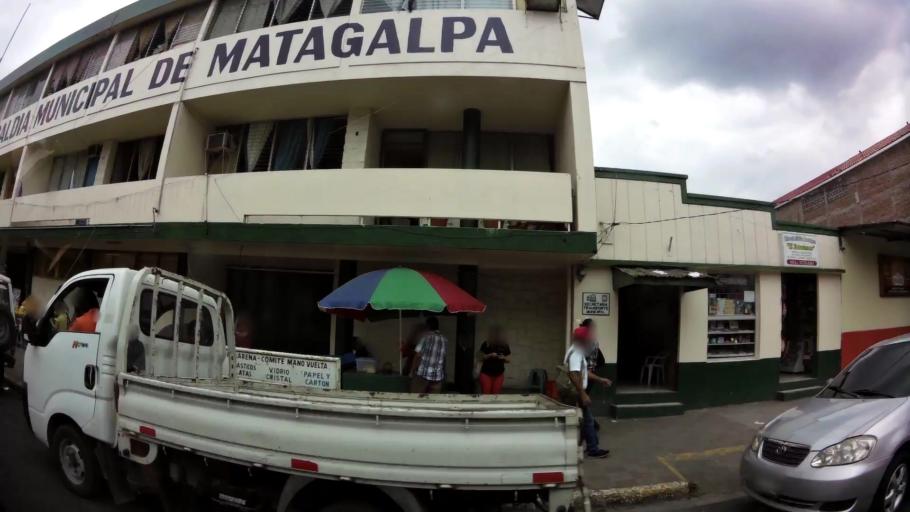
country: NI
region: Matagalpa
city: Matagalpa
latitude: 12.9251
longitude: -85.9192
